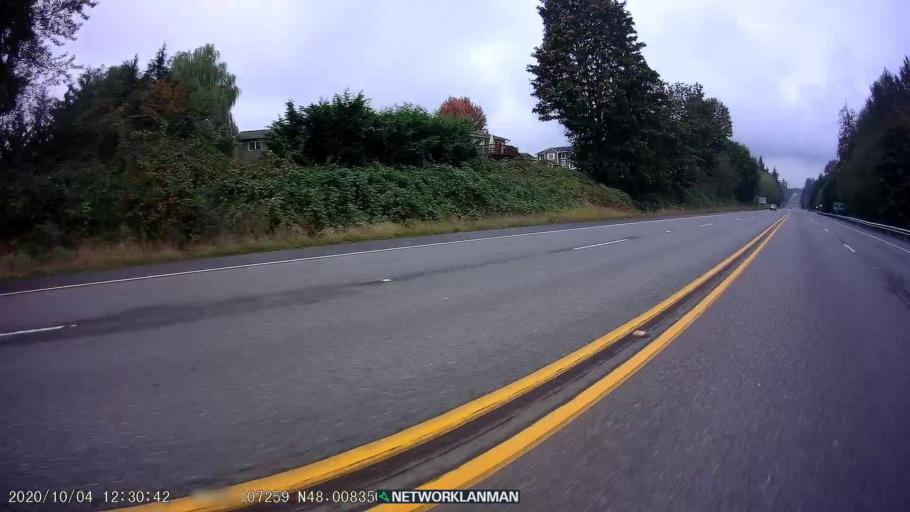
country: US
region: Washington
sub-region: Snohomish County
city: West Lake Stevens
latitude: 48.0130
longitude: -122.1008
